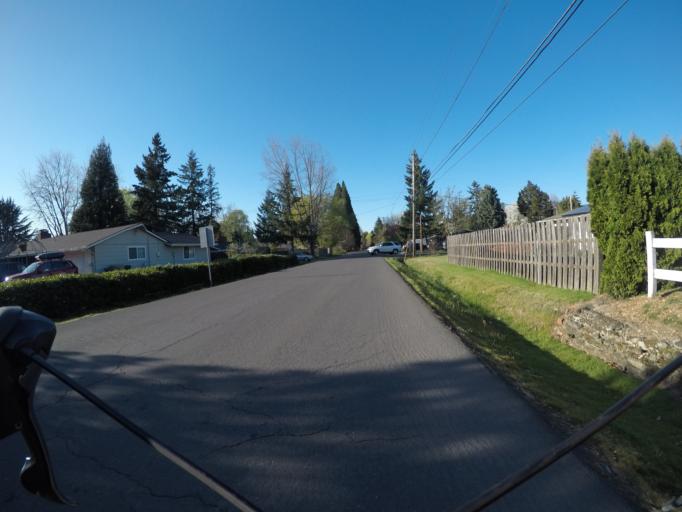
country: US
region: Oregon
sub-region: Washington County
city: Aloha
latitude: 45.4811
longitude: -122.8751
